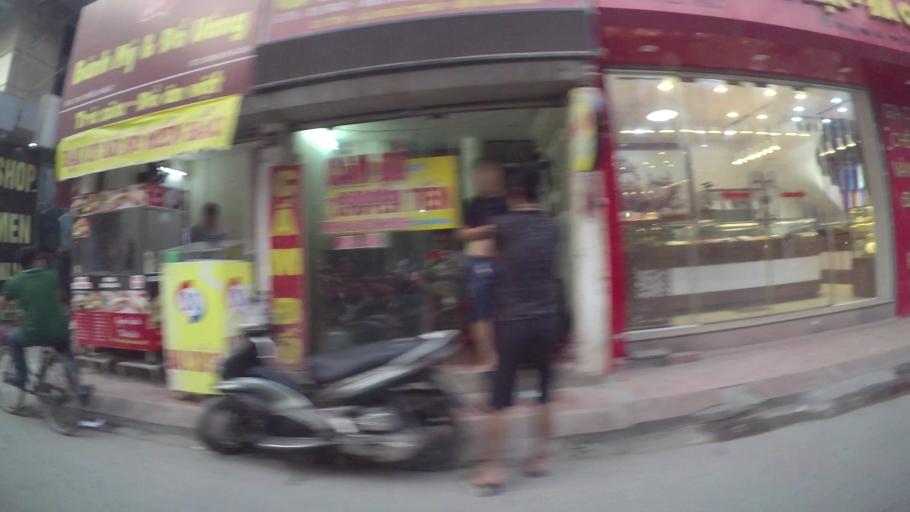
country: VN
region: Ha Noi
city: Thanh Xuan
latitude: 20.9862
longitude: 105.7982
